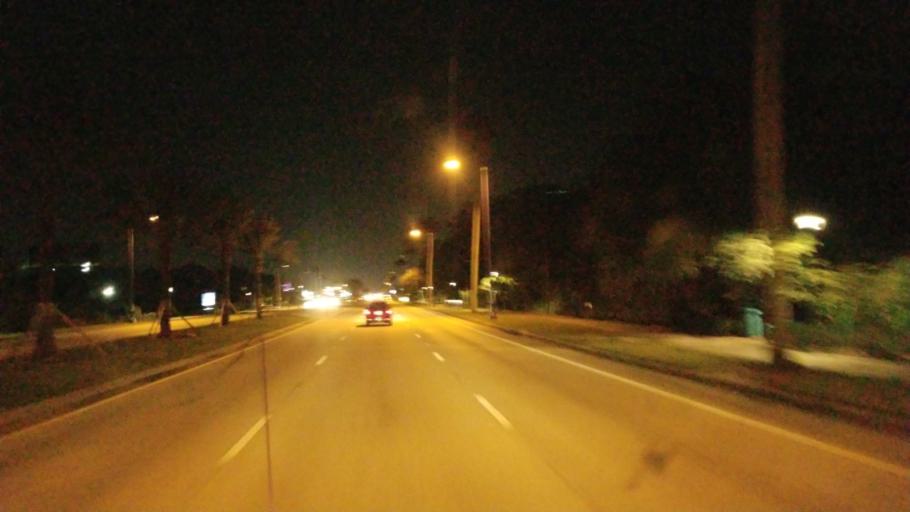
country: US
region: Florida
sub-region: Osceola County
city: Celebration
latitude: 28.3327
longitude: -81.5094
